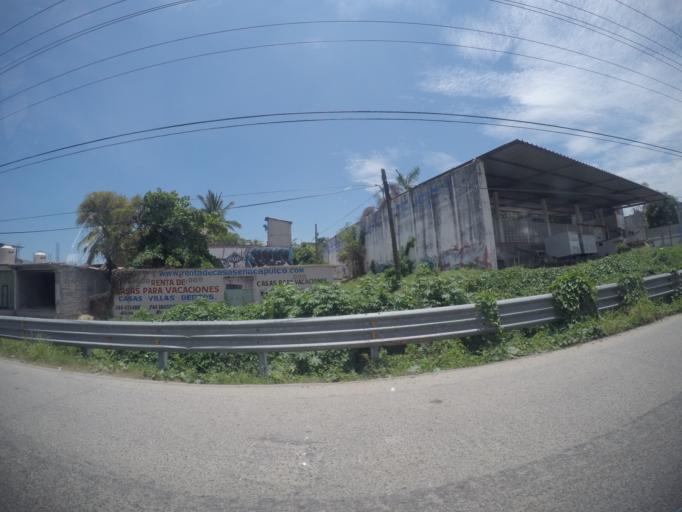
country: MX
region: Guerrero
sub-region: Acapulco de Juarez
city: Colonia Nueva Revolucion
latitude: 16.9164
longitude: -99.8203
